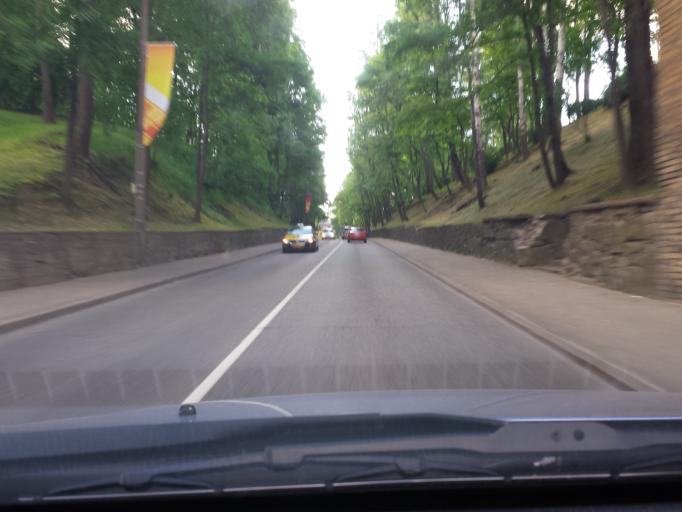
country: LV
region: Riga
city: Riga
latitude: 56.9598
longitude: 24.0683
